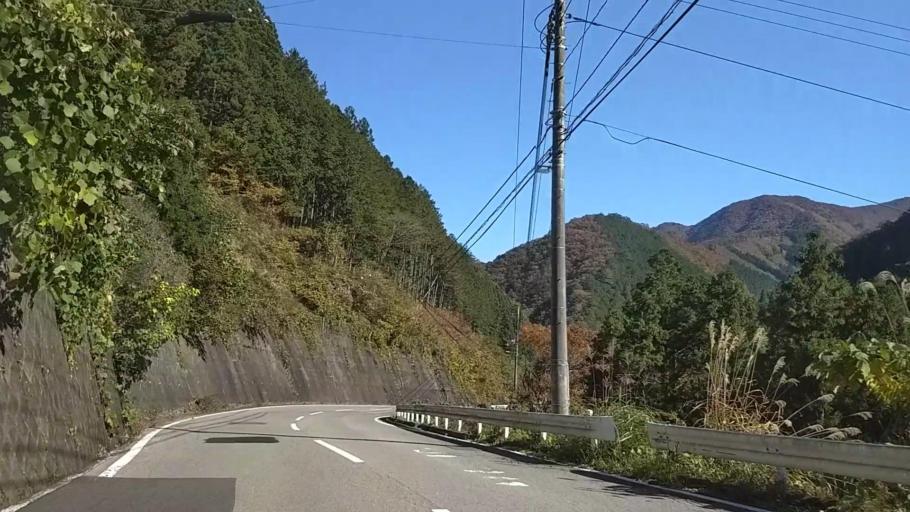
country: JP
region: Yamanashi
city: Otsuki
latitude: 35.7605
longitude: 138.9742
